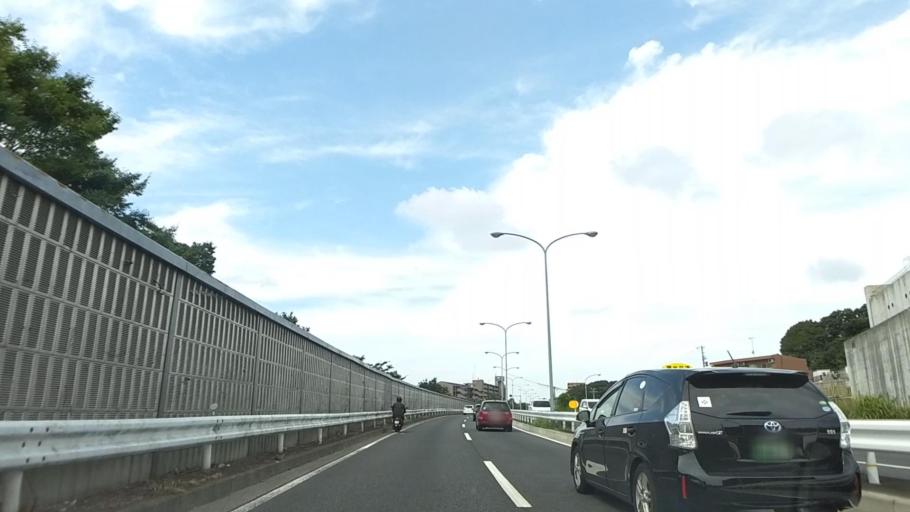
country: JP
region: Kanagawa
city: Yokohama
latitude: 35.4807
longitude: 139.5844
